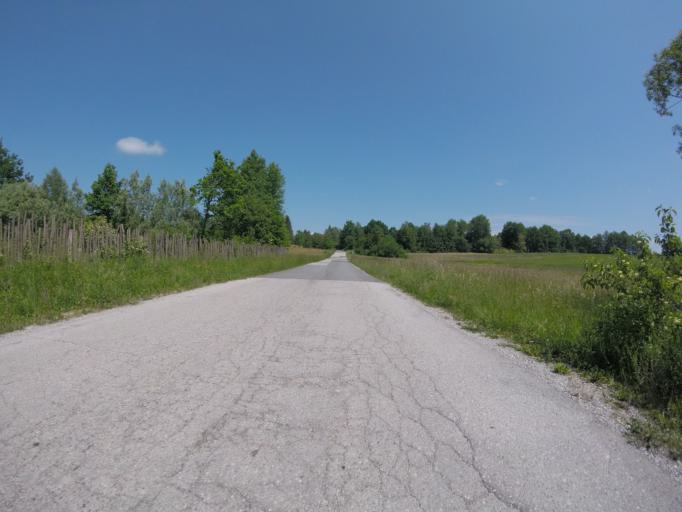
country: HR
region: Grad Zagreb
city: Strmec
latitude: 45.5683
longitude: 15.9465
